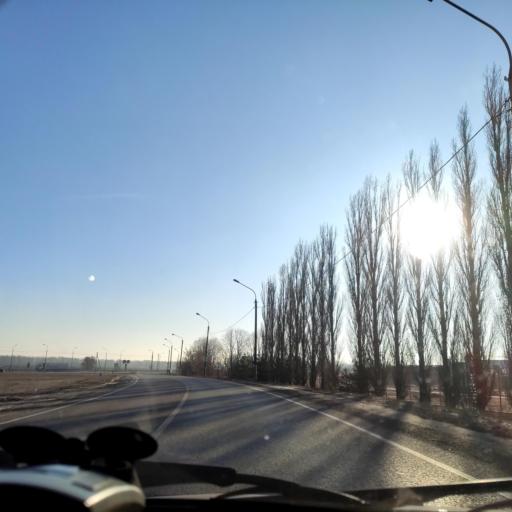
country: RU
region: Voronezj
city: Ramon'
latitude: 51.9290
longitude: 39.2179
